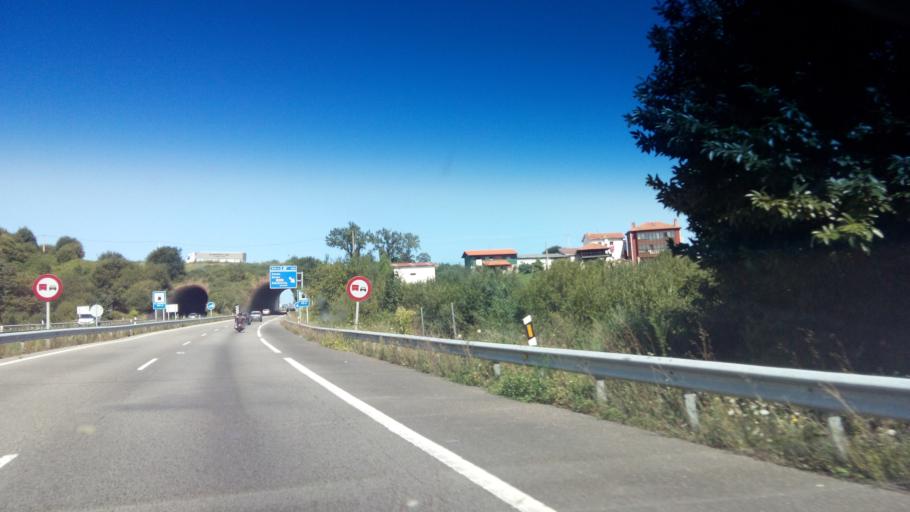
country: ES
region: Asturias
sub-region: Province of Asturias
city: Ribadesella
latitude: 43.4514
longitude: -5.1080
